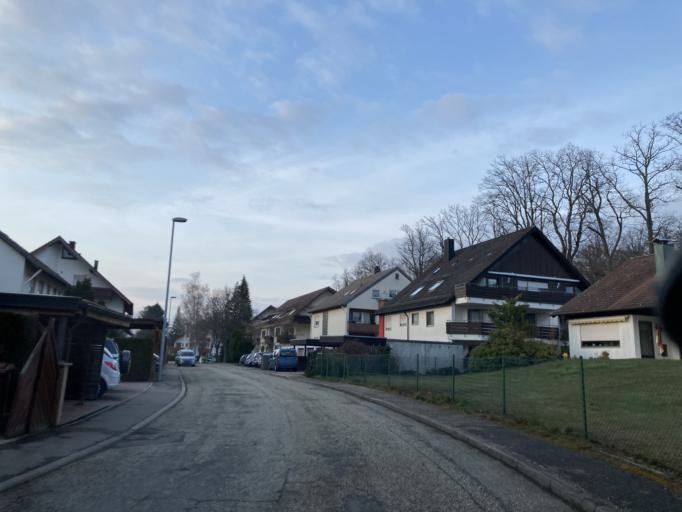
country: DE
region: Baden-Wuerttemberg
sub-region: Karlsruhe Region
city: Schomberg
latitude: 48.7833
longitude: 8.6476
